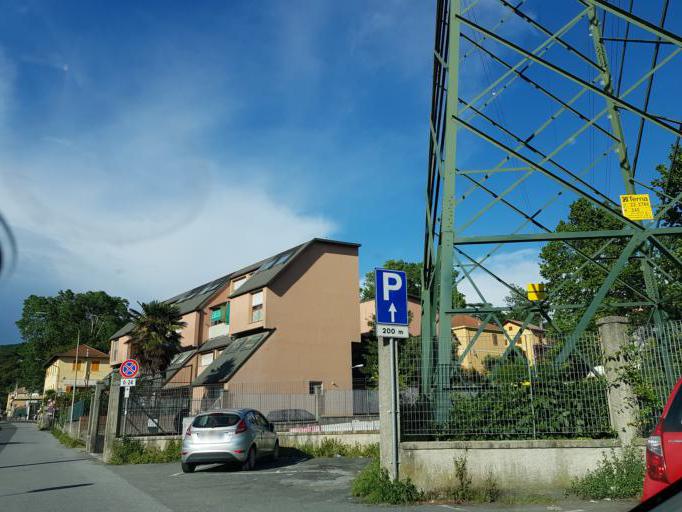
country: IT
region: Liguria
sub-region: Provincia di Genova
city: Manesseno
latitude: 44.4797
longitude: 8.9201
